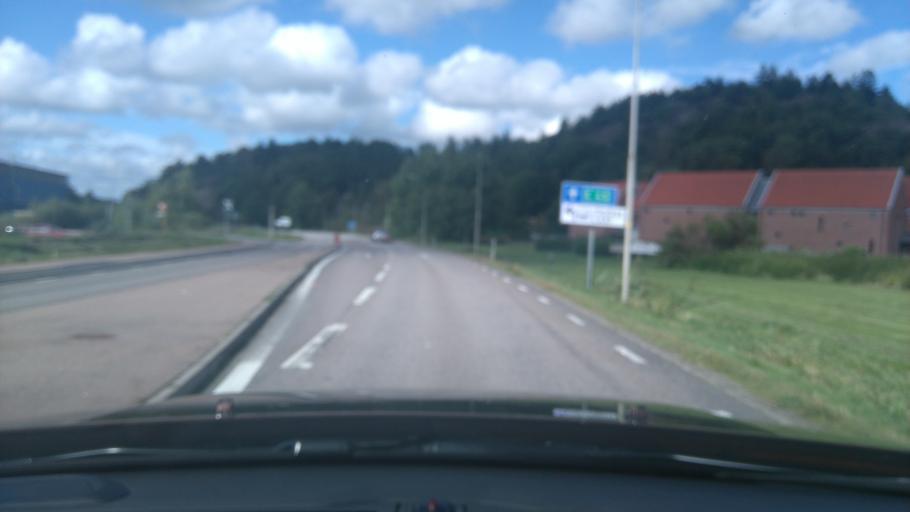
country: SE
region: Vaestra Goetaland
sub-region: Lilla Edets Kommun
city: Lodose
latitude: 58.0354
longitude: 12.1529
